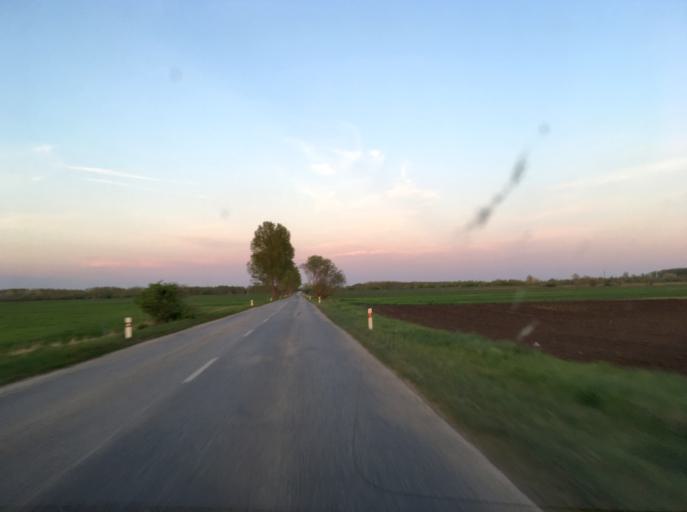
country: SK
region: Nitriansky
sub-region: Okres Nove Zamky
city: Nove Zamky
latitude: 47.9223
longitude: 18.0943
